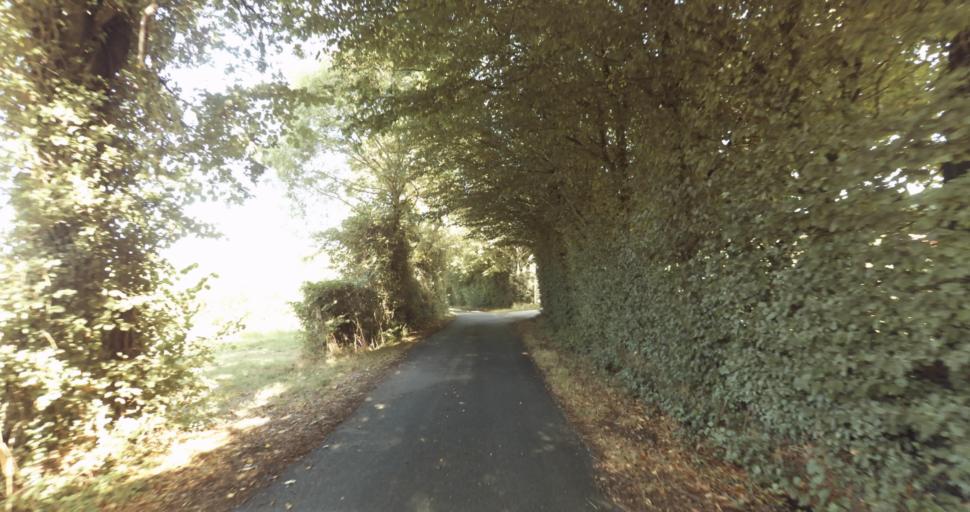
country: FR
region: Lower Normandy
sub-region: Departement de l'Orne
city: Vimoutiers
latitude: 48.9258
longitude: 0.1404
